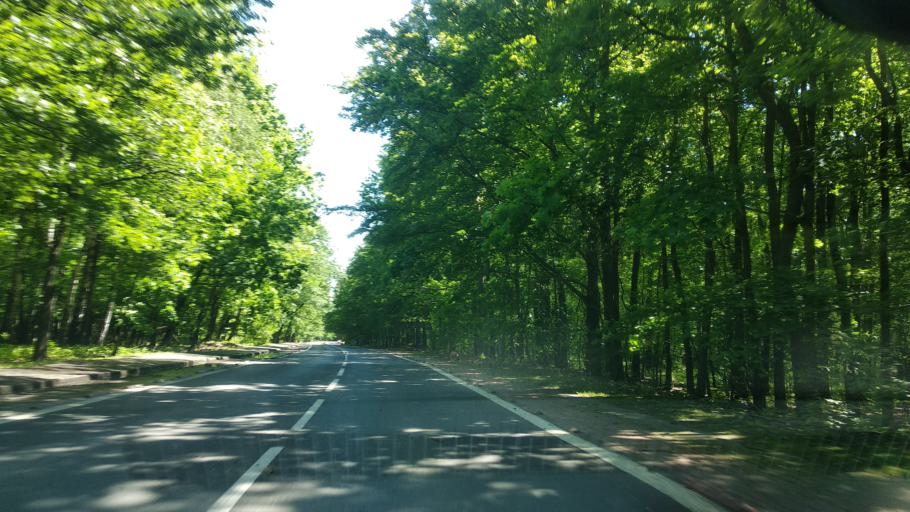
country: PL
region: Silesian Voivodeship
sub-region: Ruda Slaska
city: Ruda Slaska
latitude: 50.2363
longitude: 18.9106
